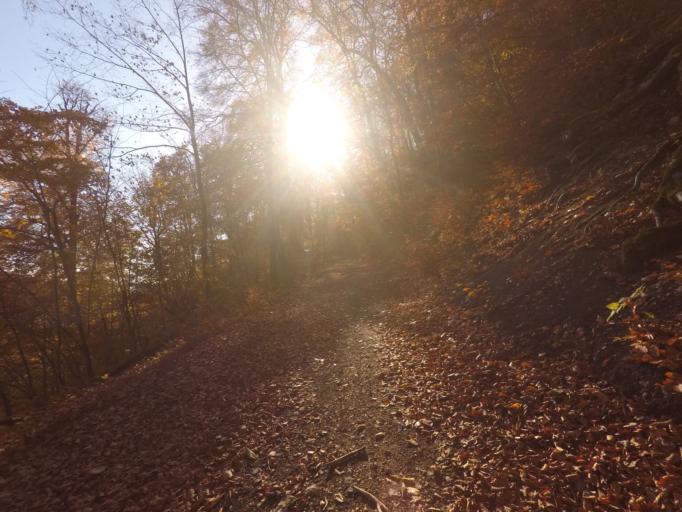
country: DE
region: Baden-Wuerttemberg
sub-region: Tuebingen Region
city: Pfullingen
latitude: 48.4398
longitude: 9.2287
